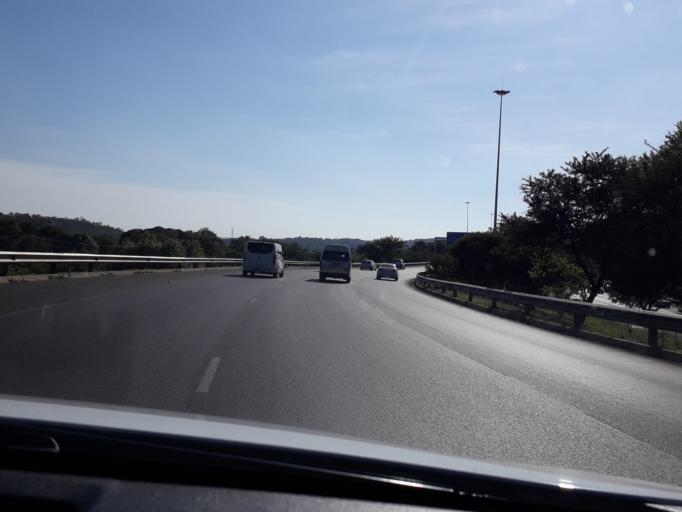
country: ZA
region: Gauteng
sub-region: City of Tshwane Metropolitan Municipality
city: Pretoria
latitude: -25.7423
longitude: 28.2503
